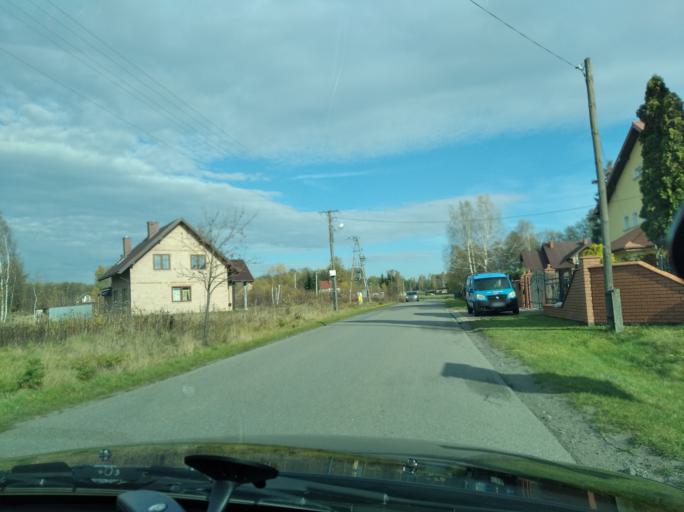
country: PL
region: Subcarpathian Voivodeship
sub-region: Powiat ropczycko-sedziszowski
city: Sedziszow Malopolski
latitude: 50.0990
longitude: 21.6595
